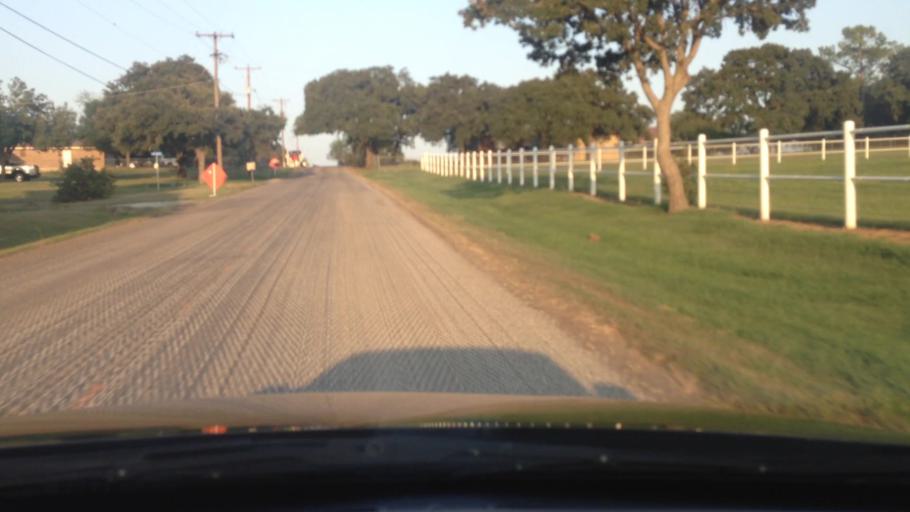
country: US
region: Texas
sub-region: Tarrant County
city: Rendon
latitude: 32.6017
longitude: -97.2354
